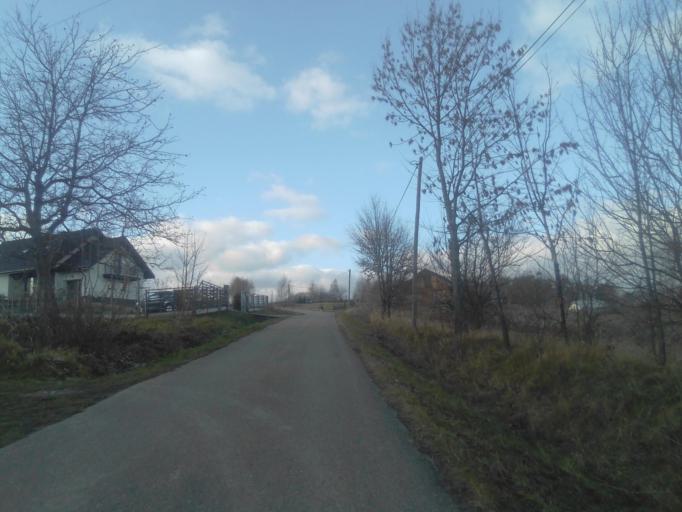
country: PL
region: Subcarpathian Voivodeship
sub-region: Powiat strzyzowski
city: Babica
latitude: 49.9428
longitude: 21.8894
